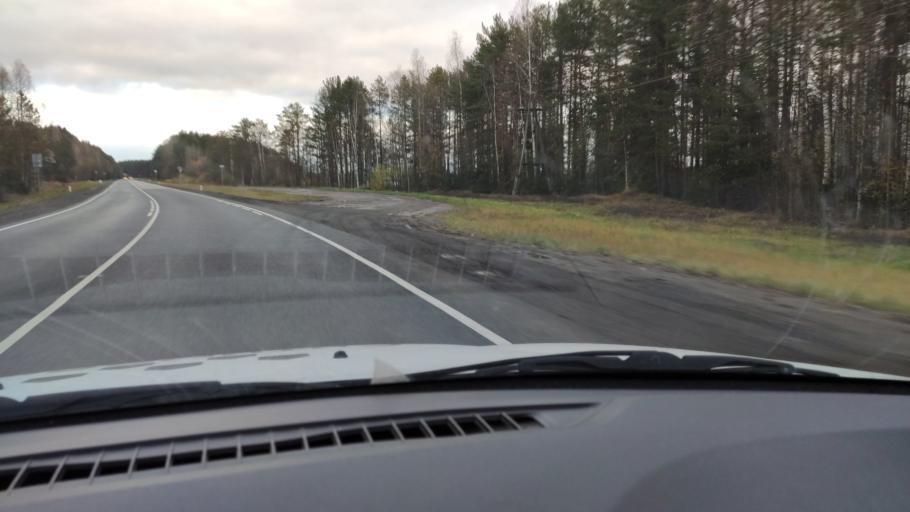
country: RU
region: Kirov
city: Belaya Kholunitsa
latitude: 58.8736
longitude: 50.8591
